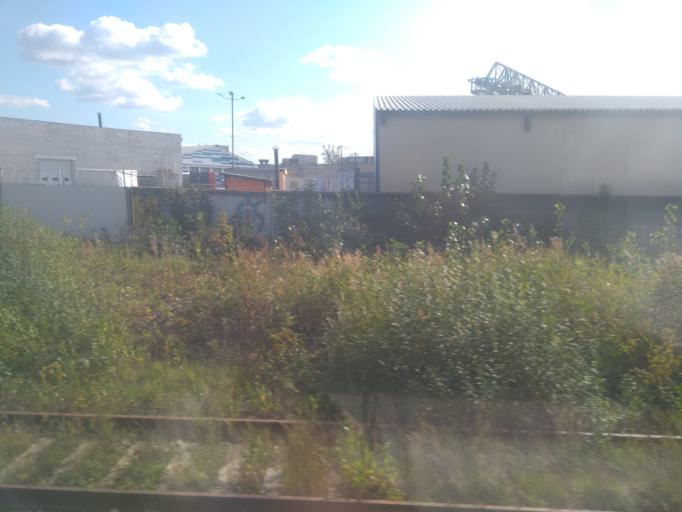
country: RU
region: Tatarstan
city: Verkhniy Uslon
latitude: 55.8049
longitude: 49.0422
